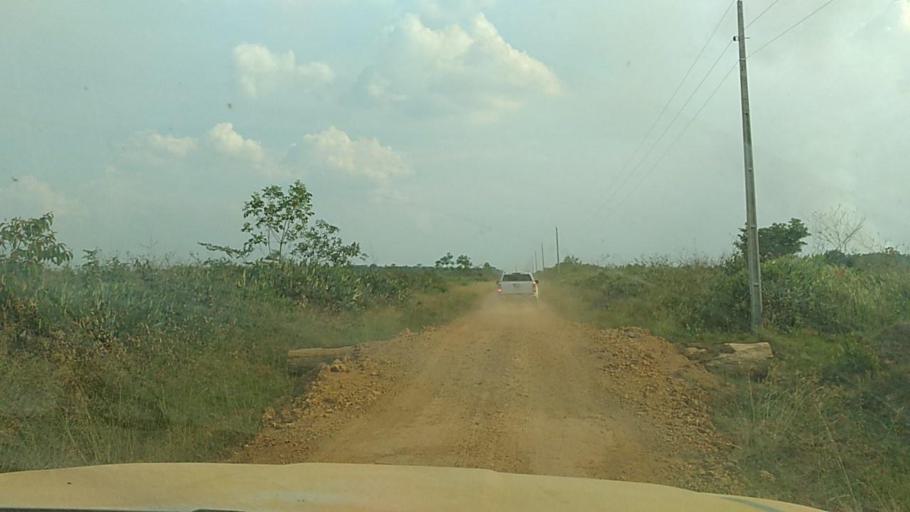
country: BR
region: Rondonia
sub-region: Porto Velho
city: Porto Velho
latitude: -8.6660
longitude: -64.0234
